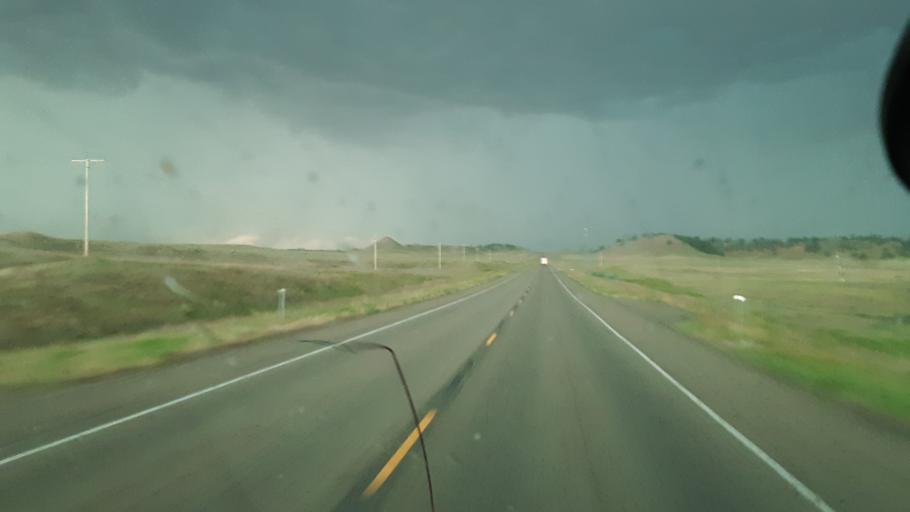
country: US
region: Montana
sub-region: Powder River County
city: Broadus
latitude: 45.4690
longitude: -105.4757
